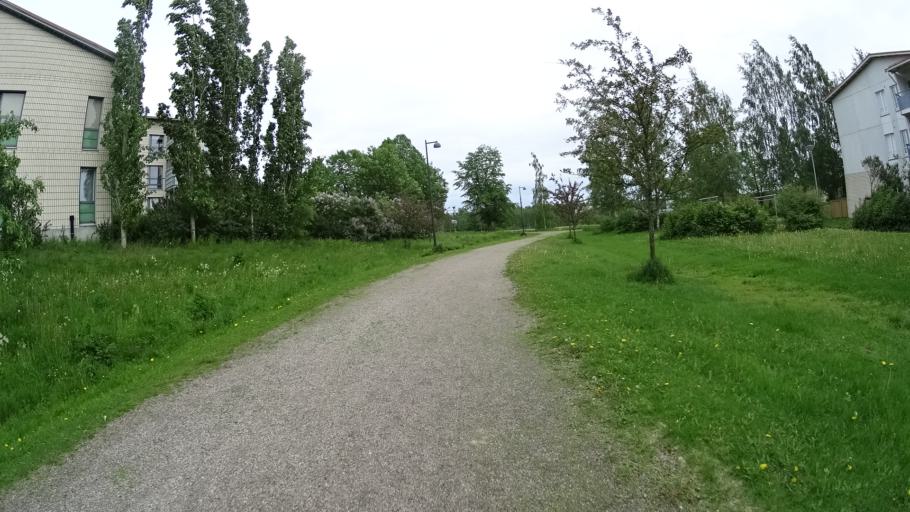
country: FI
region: Uusimaa
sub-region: Helsinki
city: Vantaa
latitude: 60.2935
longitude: 25.0589
